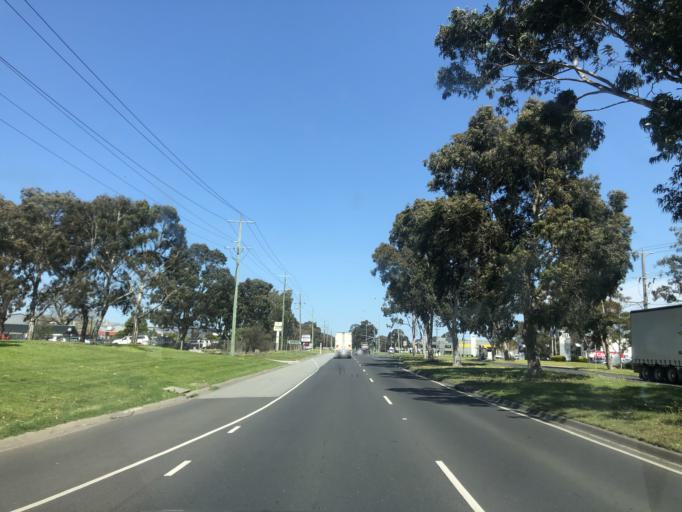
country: AU
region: Victoria
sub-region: Casey
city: Hampton Park
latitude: -38.0250
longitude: 145.2134
